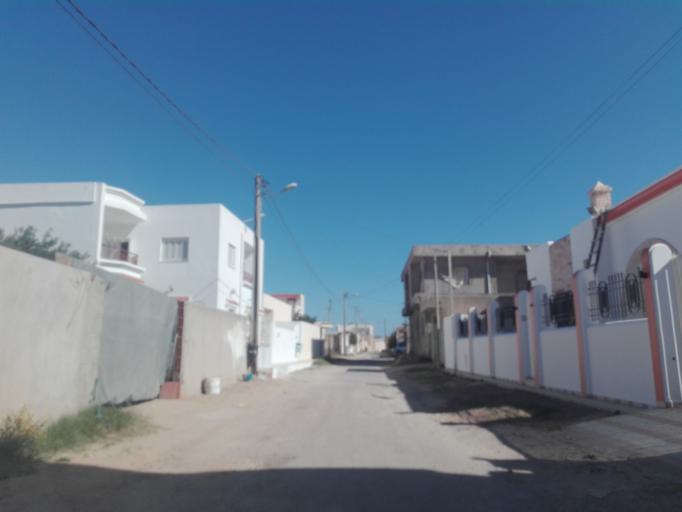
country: TN
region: Safaqis
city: Al Qarmadah
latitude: 34.7108
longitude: 11.2026
